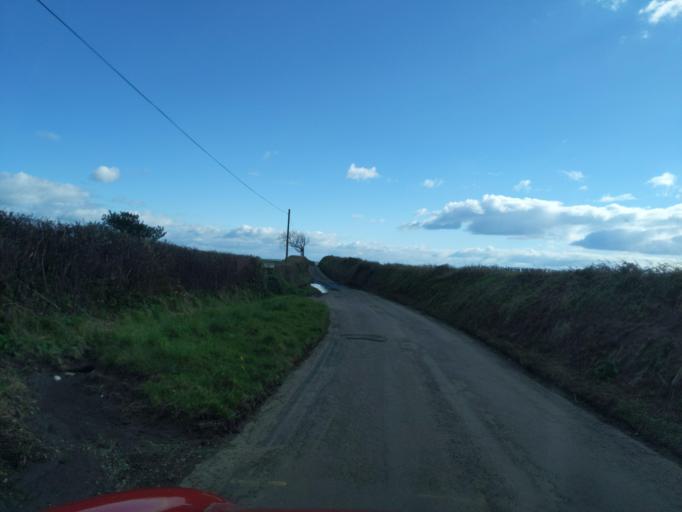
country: GB
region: England
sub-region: Devon
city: Kingsbridge
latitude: 50.2985
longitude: -3.7915
